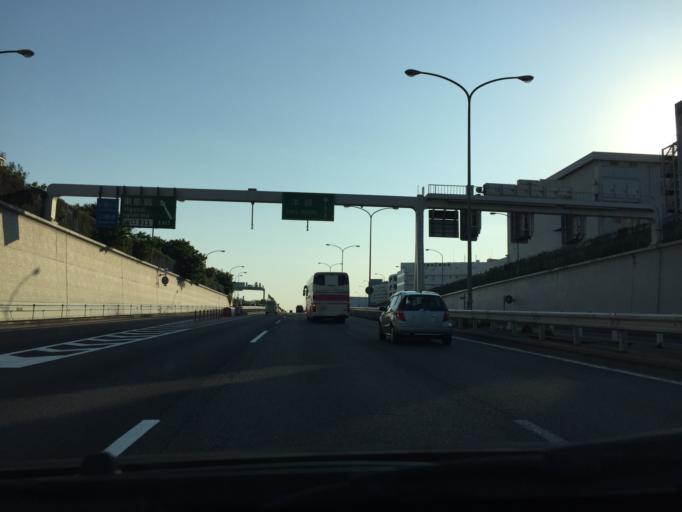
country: JP
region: Kanagawa
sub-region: Kawasaki-shi
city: Kawasaki
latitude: 35.5025
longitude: 139.7684
